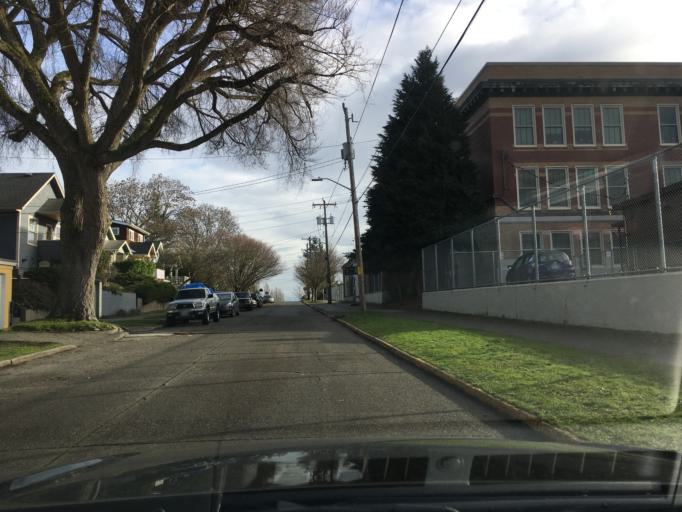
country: US
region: Washington
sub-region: King County
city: Seattle
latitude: 47.6686
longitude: -122.3274
